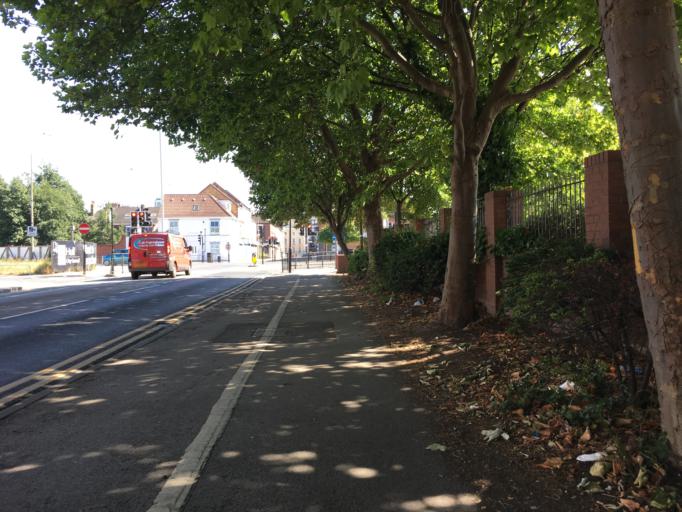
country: GB
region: England
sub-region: City of Kingston upon Hull
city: Hull
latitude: 53.7489
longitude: -0.3403
